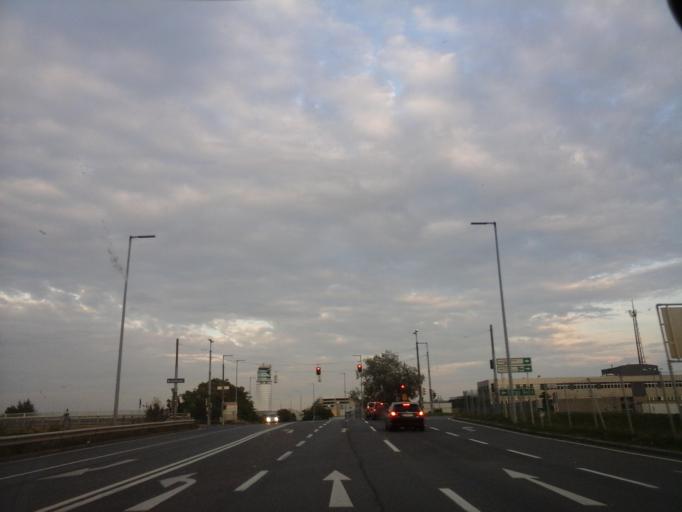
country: AT
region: Lower Austria
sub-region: Politischer Bezirk Wien-Umgebung
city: Rauchenwarth
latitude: 48.1273
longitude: 16.5480
